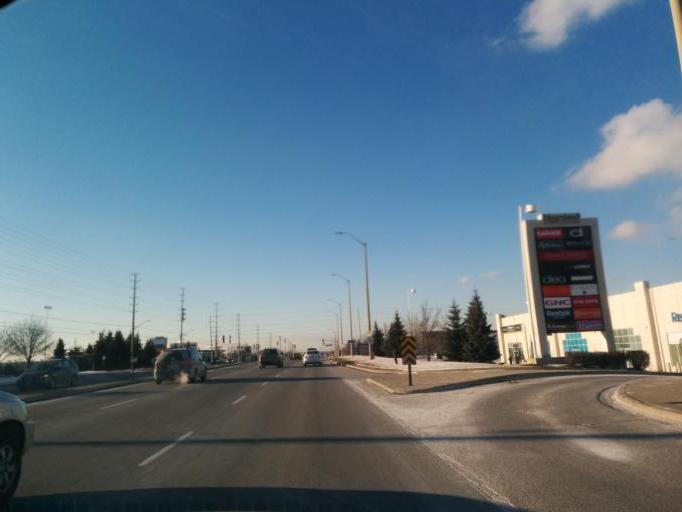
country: CA
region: Ontario
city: Mississauga
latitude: 43.6127
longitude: -79.6964
